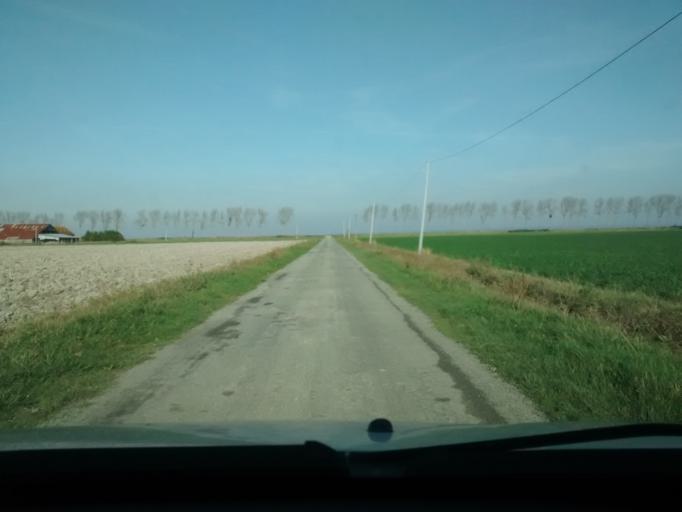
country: FR
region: Brittany
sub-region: Departement d'Ille-et-Vilaine
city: Roz-sur-Couesnon
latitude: 48.6155
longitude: -1.5815
